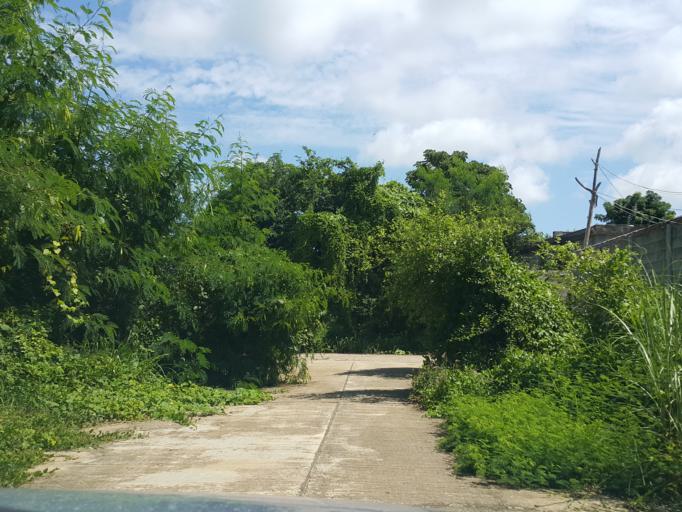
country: TH
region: Chiang Mai
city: San Kamphaeng
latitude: 18.7257
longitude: 99.0962
